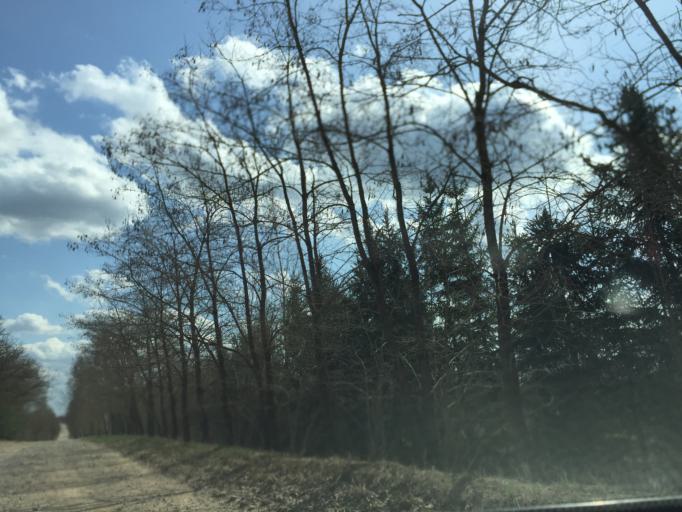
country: LV
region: Skriveri
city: Skriveri
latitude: 56.7509
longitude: 25.0853
